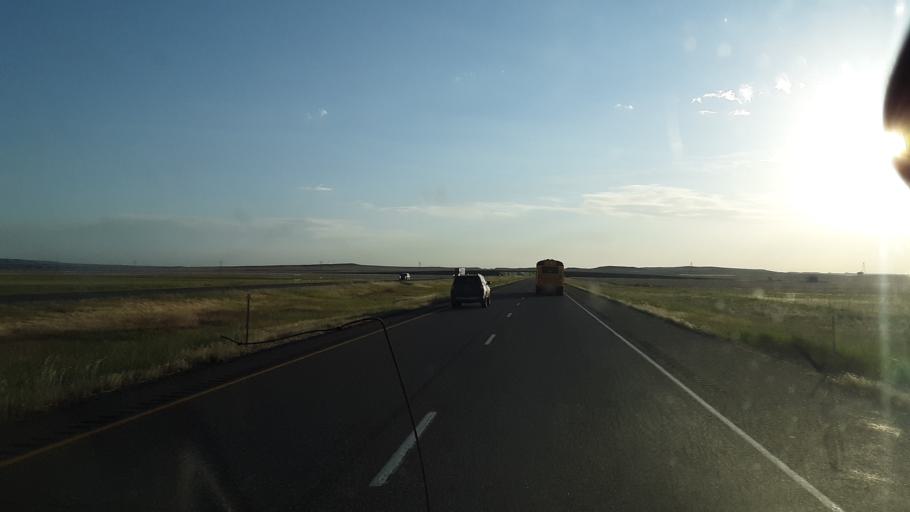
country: US
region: Montana
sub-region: Big Horn County
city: Hardin
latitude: 45.7463
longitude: -107.6691
